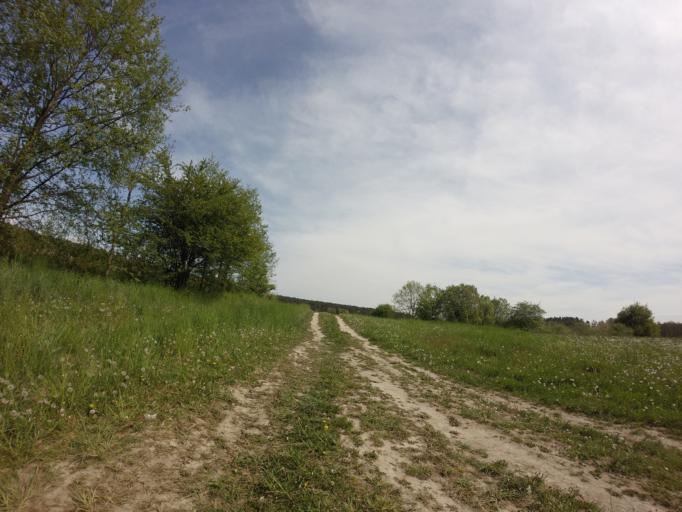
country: PL
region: West Pomeranian Voivodeship
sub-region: Powiat choszczenski
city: Choszczno
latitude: 53.2178
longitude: 15.4157
